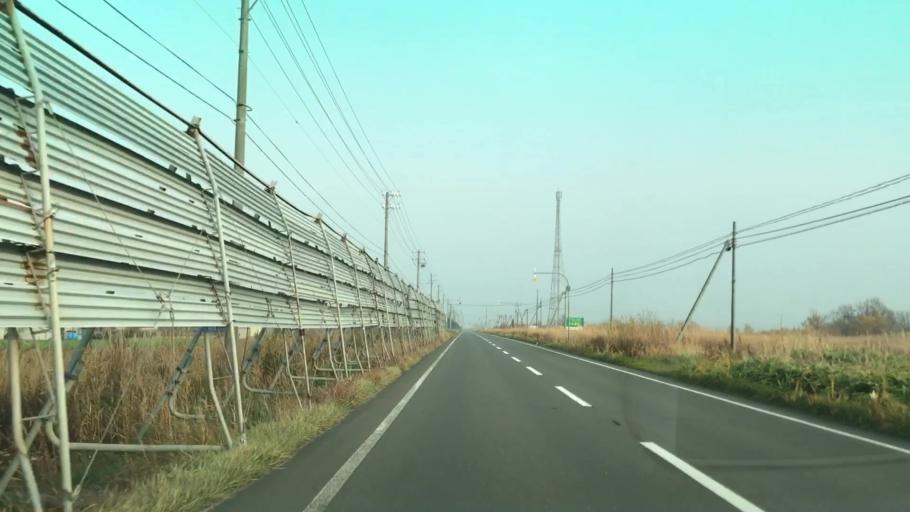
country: JP
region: Hokkaido
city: Ishikari
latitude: 43.2885
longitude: 141.4097
